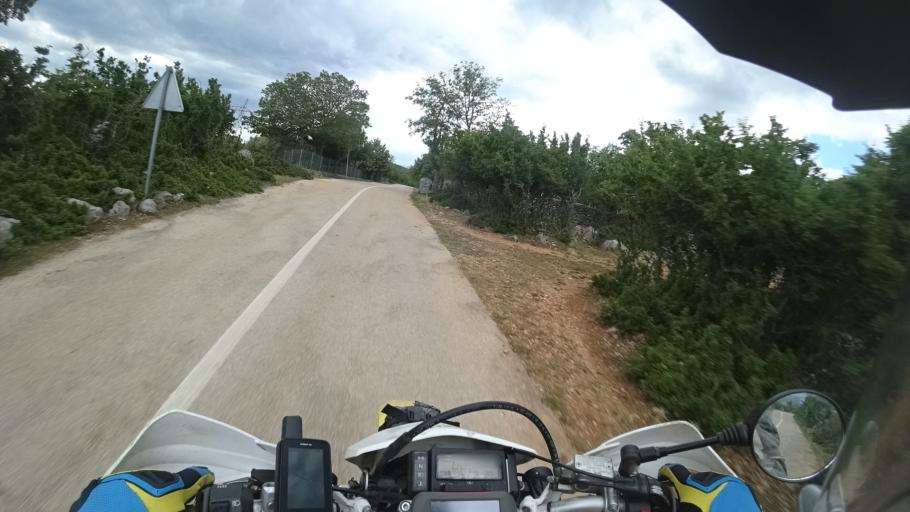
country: HR
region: Zadarska
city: Gracac
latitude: 44.1988
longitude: 15.8709
